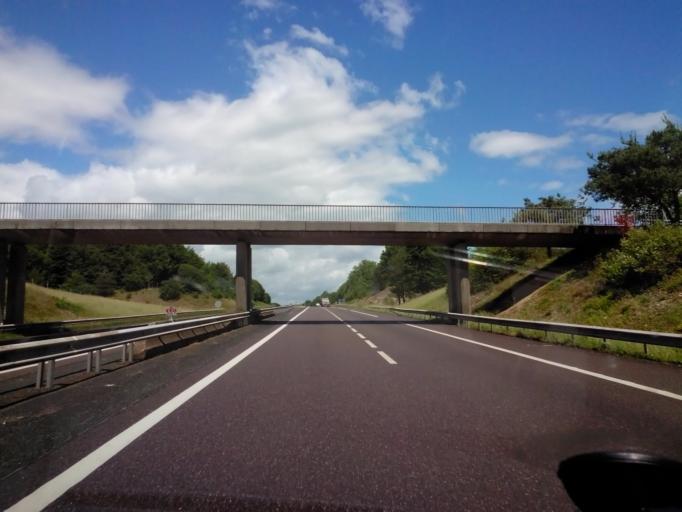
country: FR
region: Lorraine
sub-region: Departement de Meurthe-et-Moselle
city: Colombey-les-Belles
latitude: 48.5014
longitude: 5.9102
